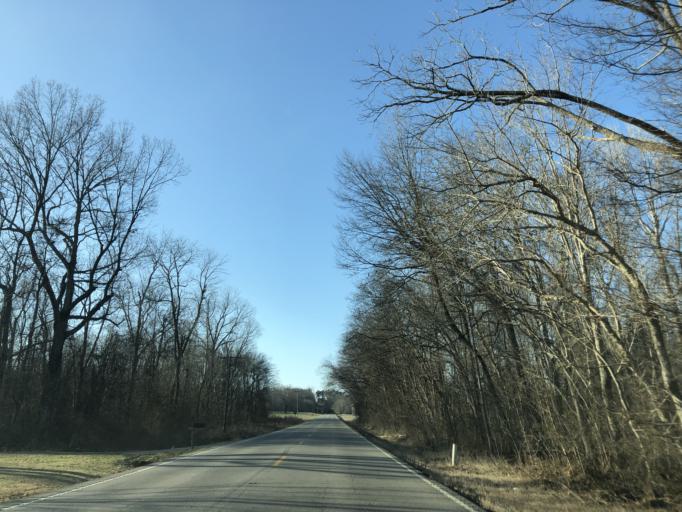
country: US
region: Tennessee
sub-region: Sumner County
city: White House
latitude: 36.5237
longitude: -86.6295
